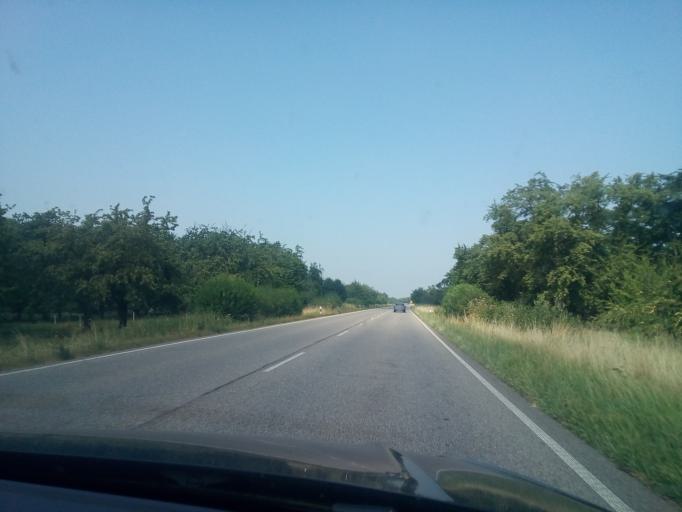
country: DE
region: Baden-Wuerttemberg
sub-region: Freiburg Region
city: Achern
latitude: 48.6053
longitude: 8.0843
